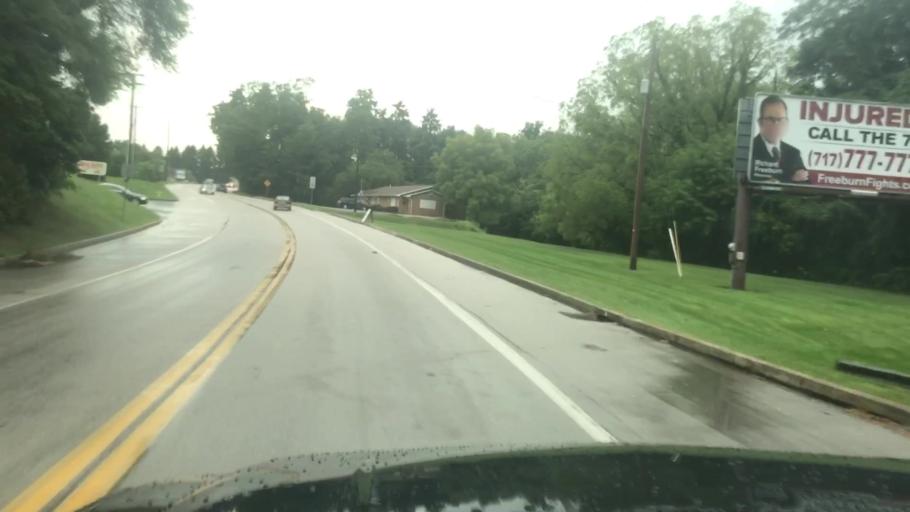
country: US
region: Pennsylvania
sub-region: Cumberland County
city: Shiremanstown
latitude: 40.2180
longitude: -76.9376
